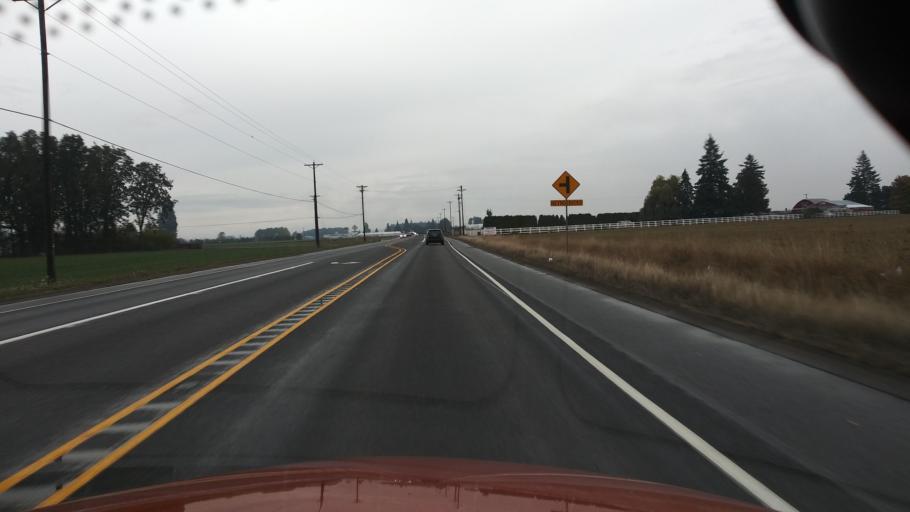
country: US
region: Oregon
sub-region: Washington County
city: Cornelius
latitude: 45.5622
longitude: -123.0551
